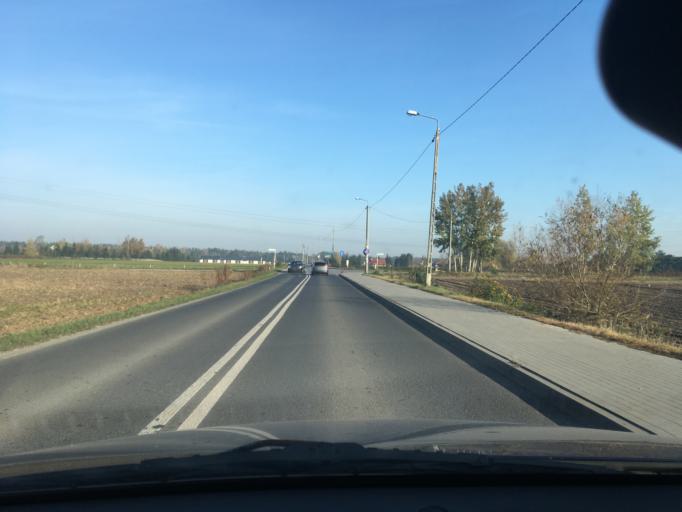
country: PL
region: Masovian Voivodeship
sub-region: Powiat piaseczynski
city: Lesznowola
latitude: 52.0694
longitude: 20.9346
